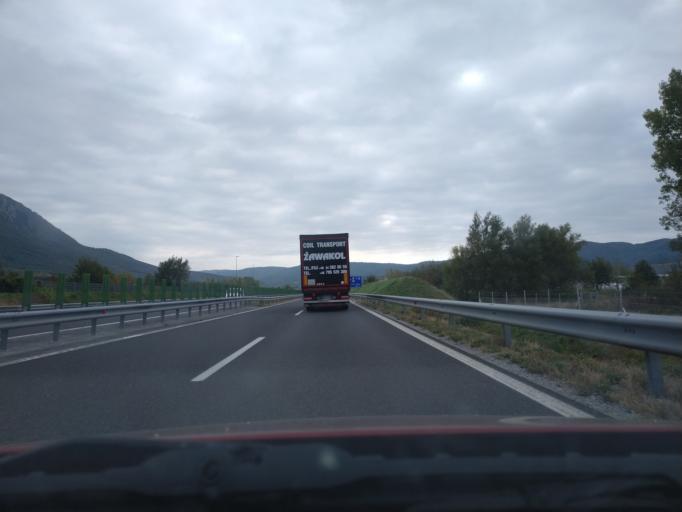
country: SI
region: Vipava
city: Vipava
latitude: 45.8388
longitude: 13.9530
